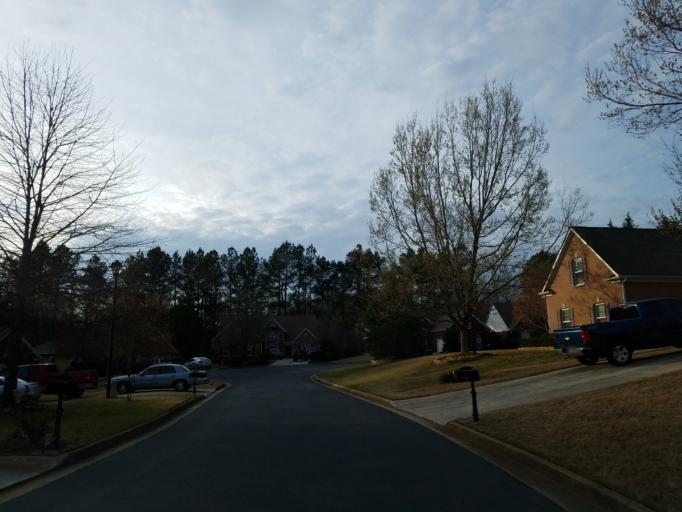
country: US
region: Georgia
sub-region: Dawson County
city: Dawsonville
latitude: 34.4293
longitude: -84.1276
